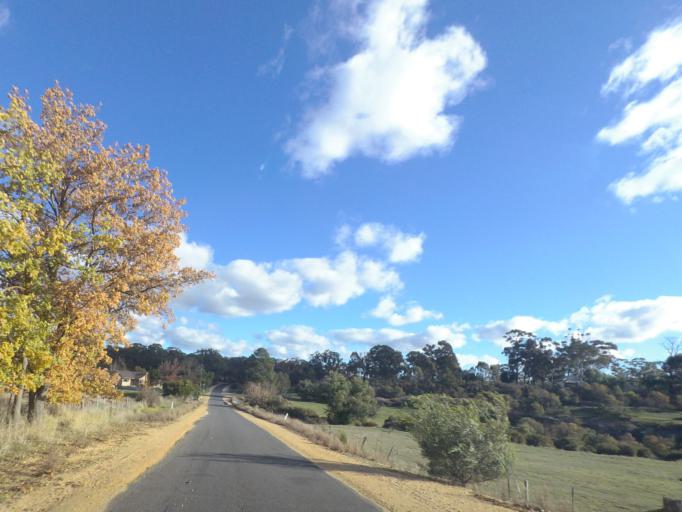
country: AU
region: Victoria
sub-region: Mount Alexander
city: Castlemaine
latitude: -37.1470
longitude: 144.2384
